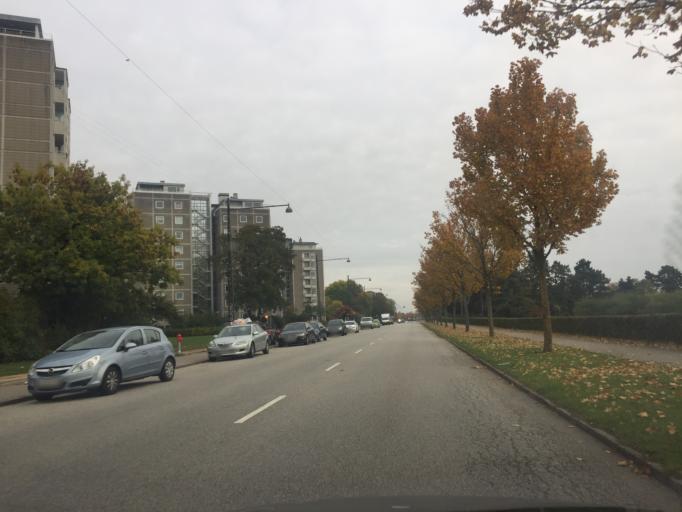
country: DK
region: Capital Region
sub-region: Kobenhavn
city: Vanlose
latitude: 55.6986
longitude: 12.5081
